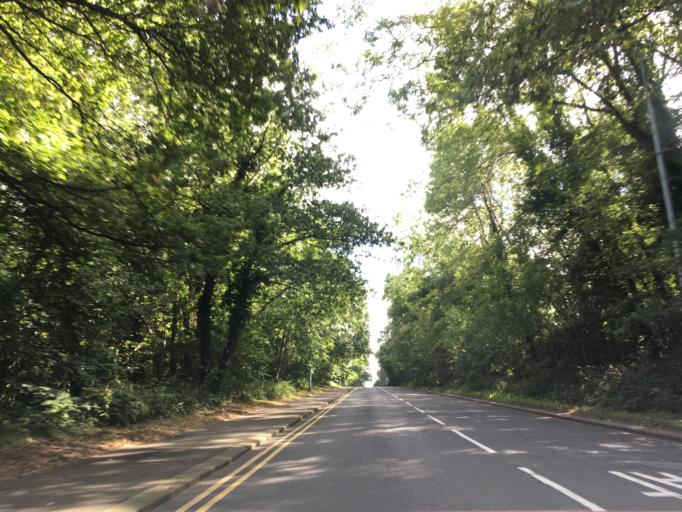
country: GB
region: Wales
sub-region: Cardiff
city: Cardiff
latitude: 51.5132
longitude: -3.1585
